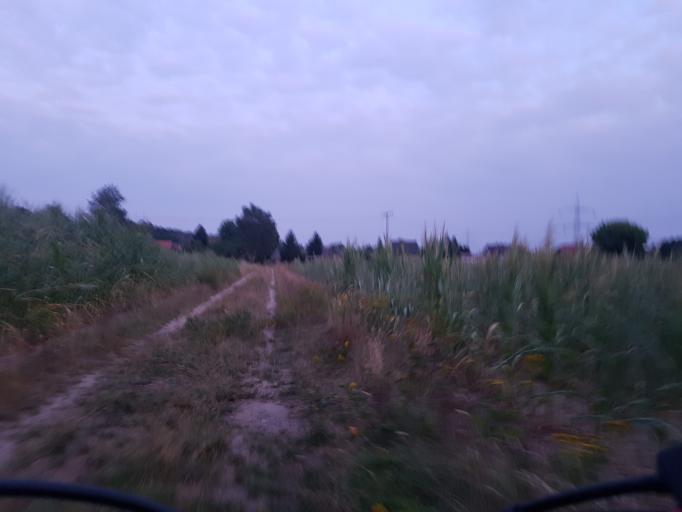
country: DE
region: Brandenburg
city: Bad Liebenwerda
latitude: 51.5431
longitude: 13.4133
